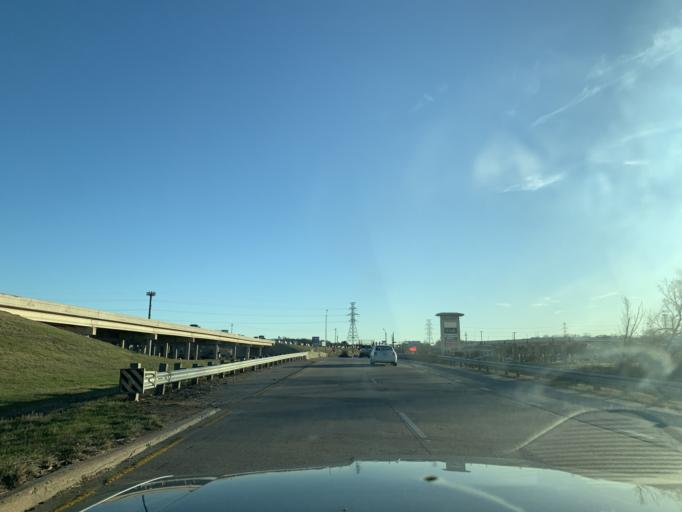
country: US
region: Texas
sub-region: Tarrant County
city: Euless
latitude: 32.8678
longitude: -97.1018
